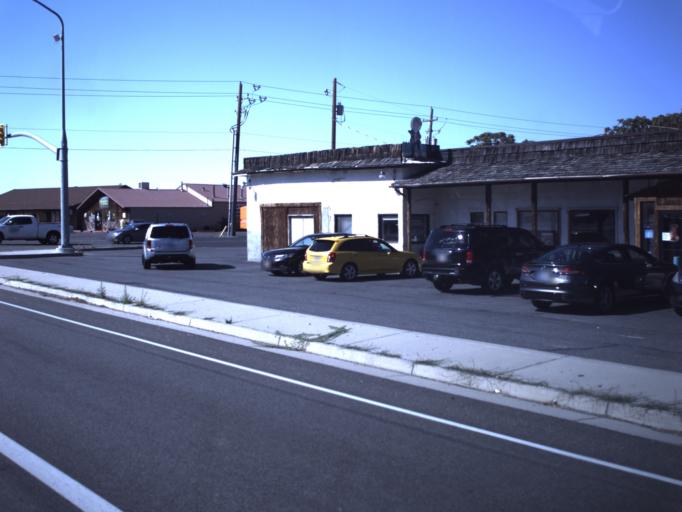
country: US
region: Utah
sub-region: Tooele County
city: Erda
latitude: 40.6024
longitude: -112.2943
